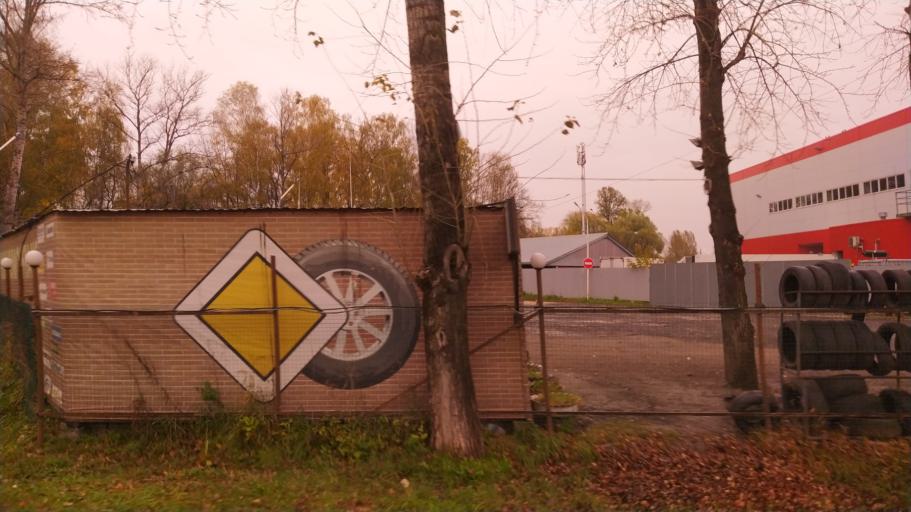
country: RU
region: Tverskaya
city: Tver
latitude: 56.8290
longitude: 35.8933
